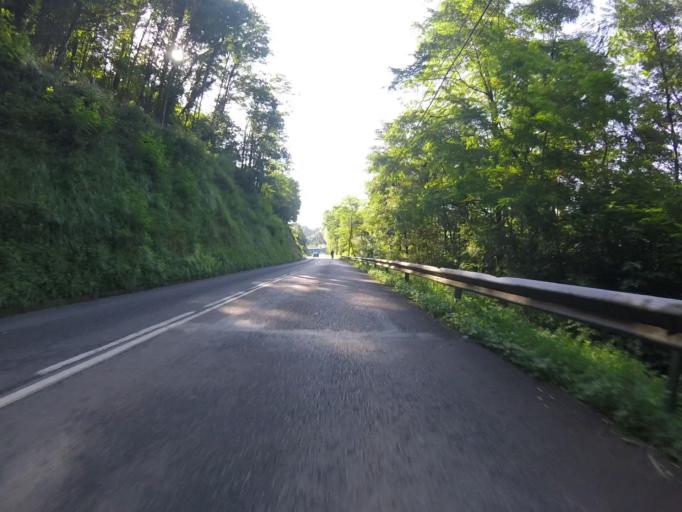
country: ES
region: Basque Country
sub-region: Provincia de Guipuzcoa
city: Asteasu
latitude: 43.1912
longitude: -2.0892
